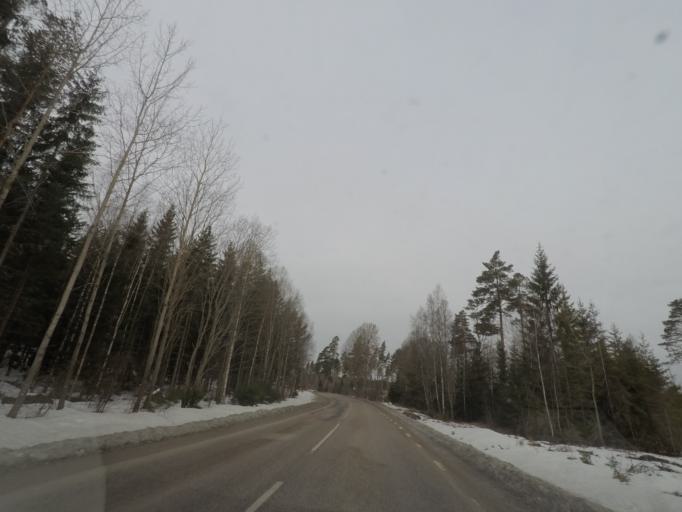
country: SE
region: Vaestmanland
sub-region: Vasteras
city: Skultuna
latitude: 59.7395
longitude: 16.3963
